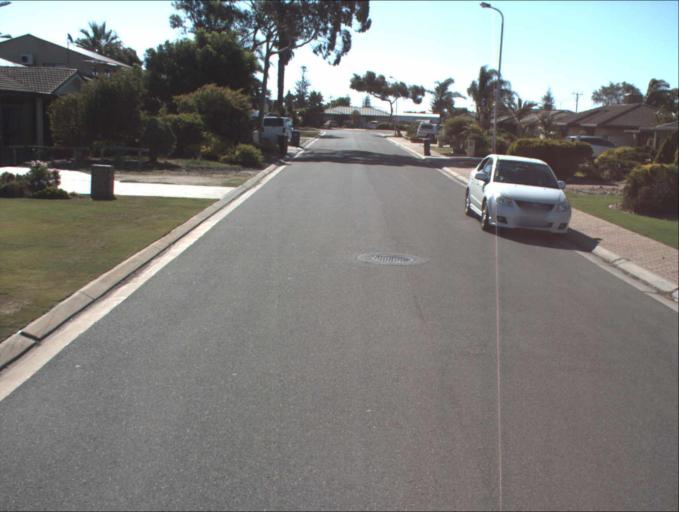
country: AU
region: South Australia
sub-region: Port Adelaide Enfield
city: Birkenhead
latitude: -34.7792
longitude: 138.4926
